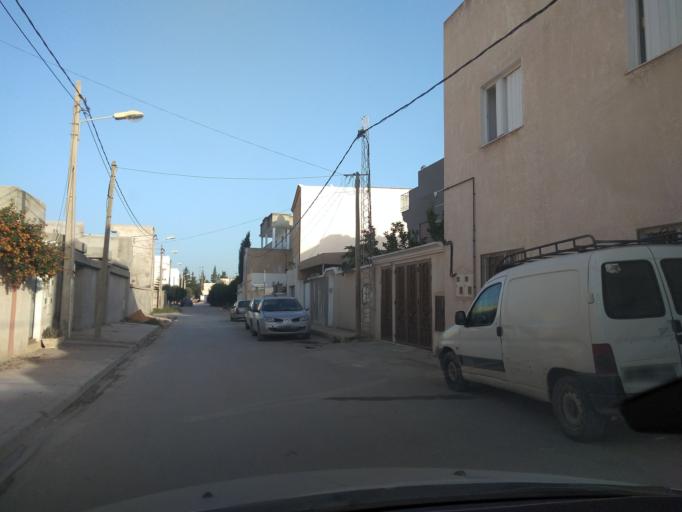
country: TN
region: Manouba
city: Manouba
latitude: 36.7938
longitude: 10.0870
